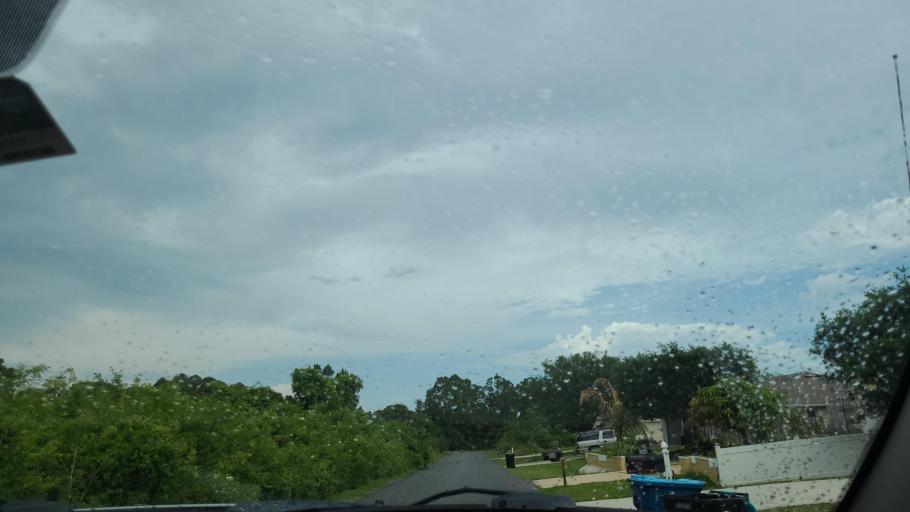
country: US
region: Florida
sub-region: Brevard County
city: Grant-Valkaria
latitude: 27.9474
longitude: -80.6439
